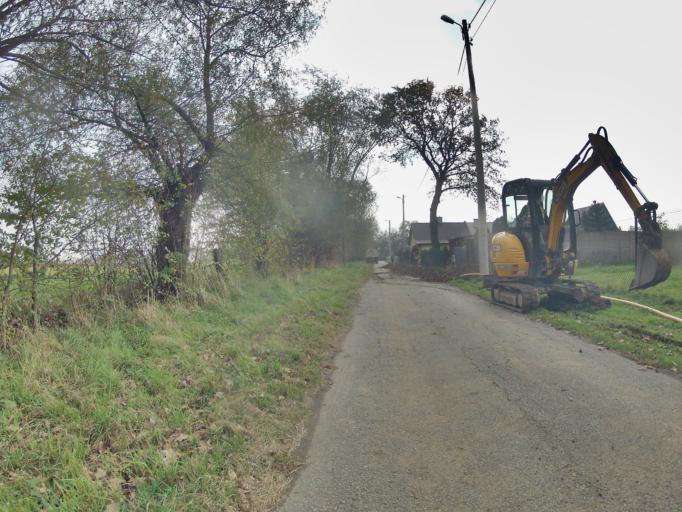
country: PL
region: Lesser Poland Voivodeship
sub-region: Powiat wielicki
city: Wegrzce Wielkie
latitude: 50.0551
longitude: 20.1125
